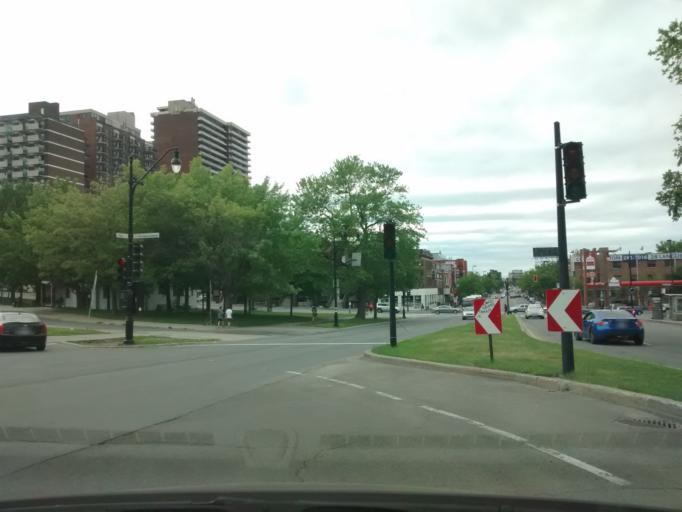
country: CA
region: Quebec
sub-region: Montreal
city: Montreal
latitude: 45.5162
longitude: -73.5880
